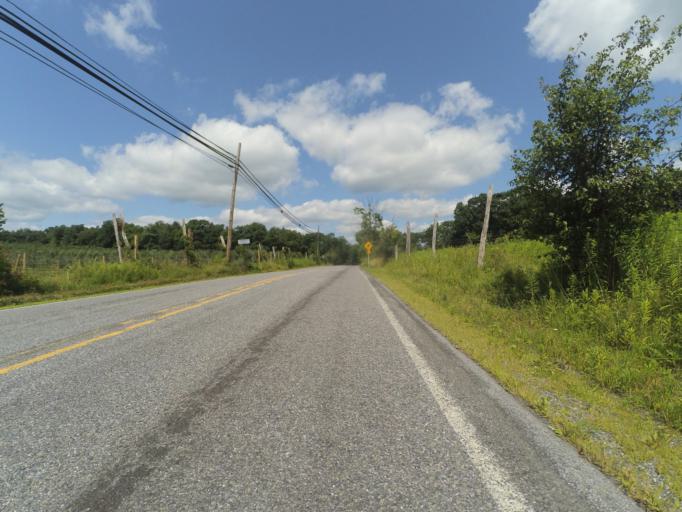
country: US
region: Pennsylvania
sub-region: Centre County
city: Stormstown
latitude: 40.7843
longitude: -78.0516
